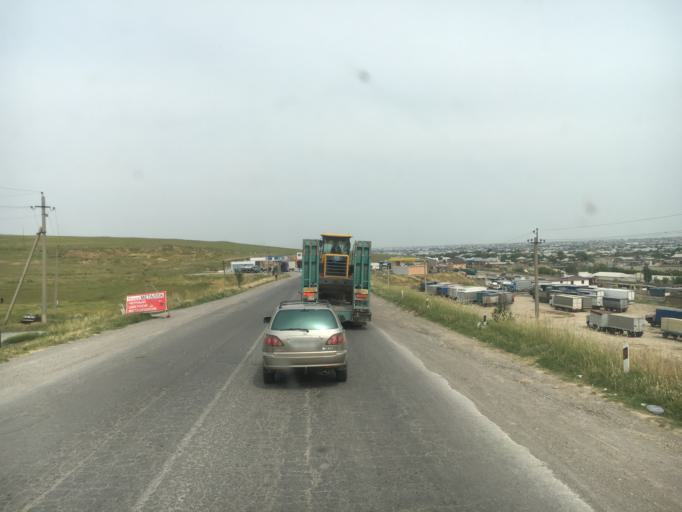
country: KZ
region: Ongtustik Qazaqstan
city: Shymkent
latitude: 42.3253
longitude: 69.5143
